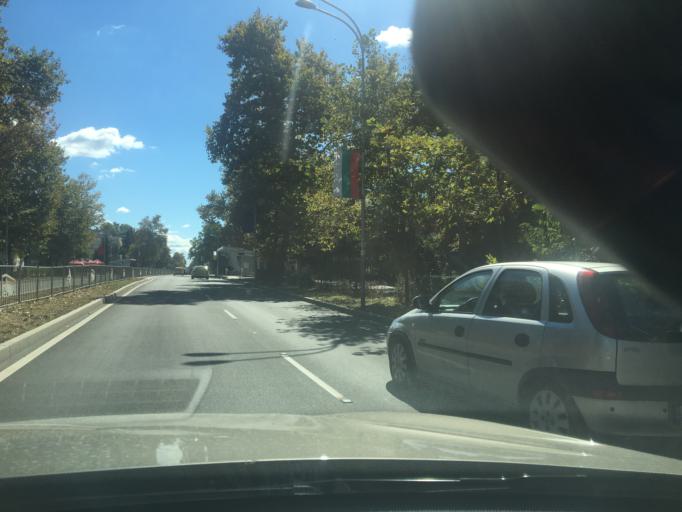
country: BG
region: Burgas
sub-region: Obshtina Burgas
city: Burgas
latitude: 42.5087
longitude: 27.4680
